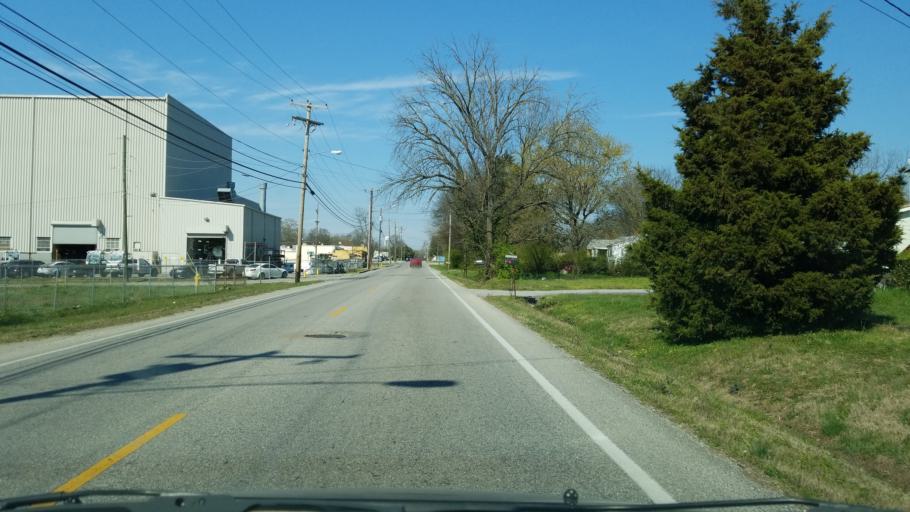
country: US
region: Tennessee
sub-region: Hamilton County
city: East Chattanooga
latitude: 35.0733
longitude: -85.2593
